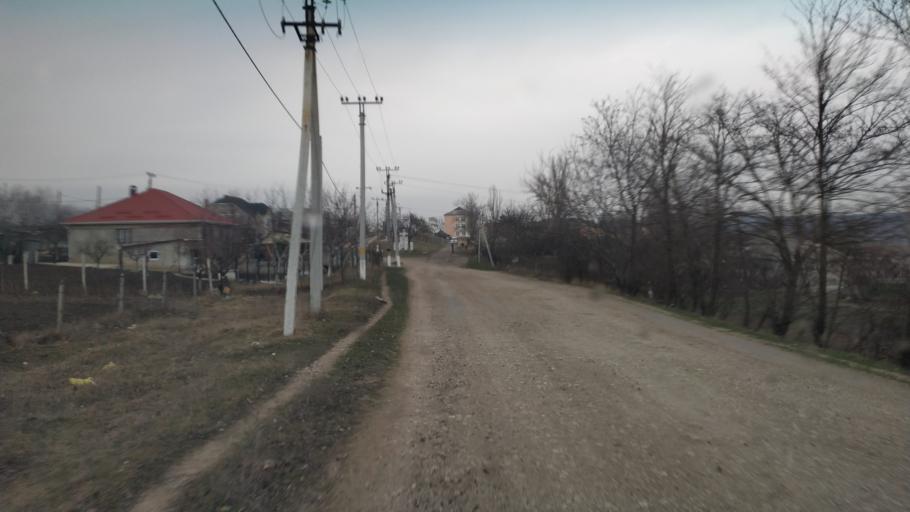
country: MD
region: Chisinau
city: Singera
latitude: 46.8297
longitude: 28.9671
